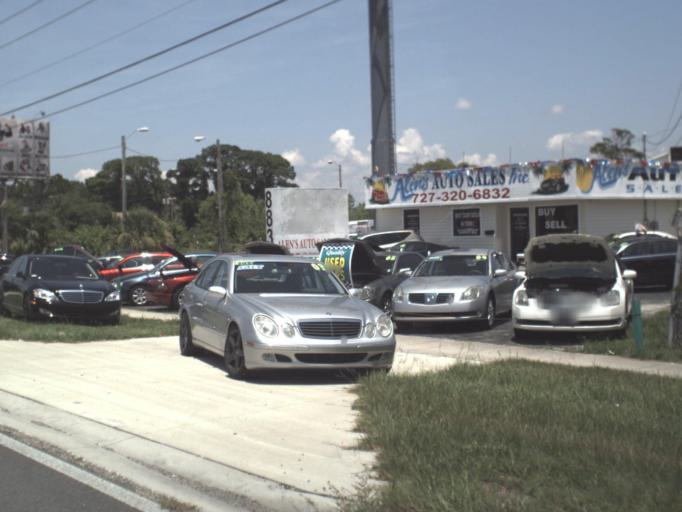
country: US
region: Florida
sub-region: Pasco County
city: Port Richey
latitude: 28.2860
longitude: -82.7138
